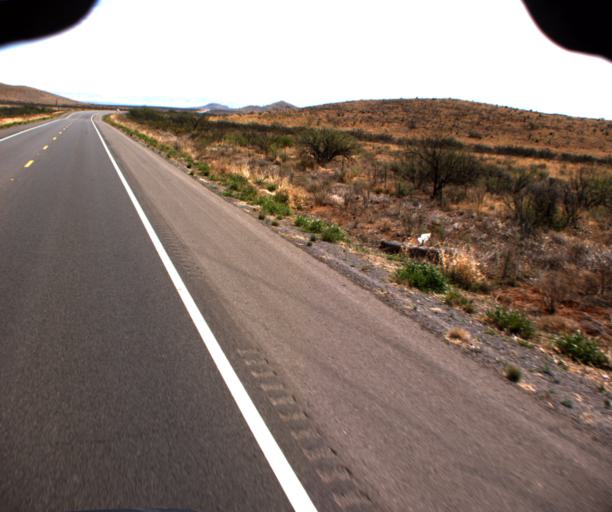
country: US
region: Arizona
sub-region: Cochise County
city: Tombstone
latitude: 31.9047
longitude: -109.7880
